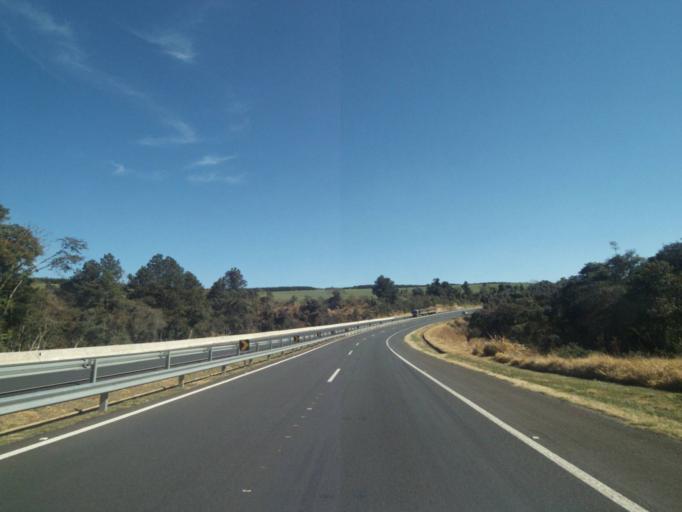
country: BR
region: Parana
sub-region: Tibagi
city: Tibagi
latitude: -24.8499
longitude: -50.4701
